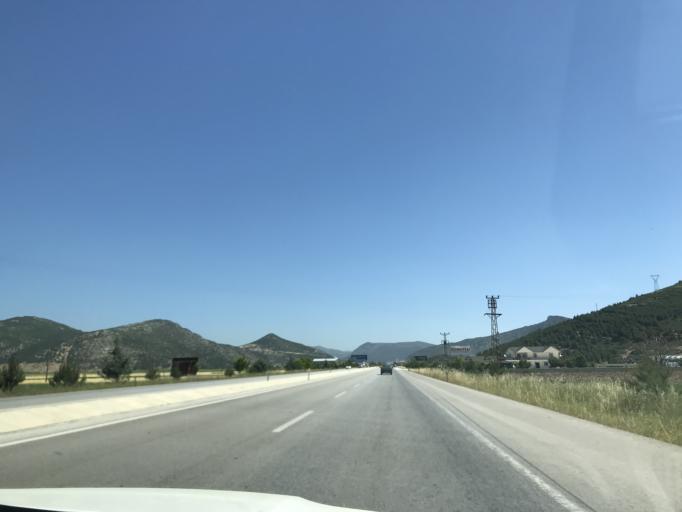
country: TR
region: Burdur
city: Bucak
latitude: 37.3835
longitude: 30.5289
